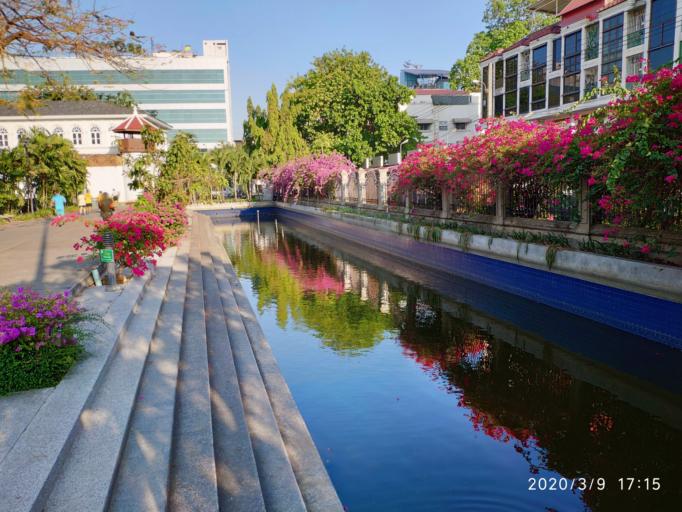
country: TH
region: Bangkok
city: Bangkok
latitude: 13.7480
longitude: 100.5026
